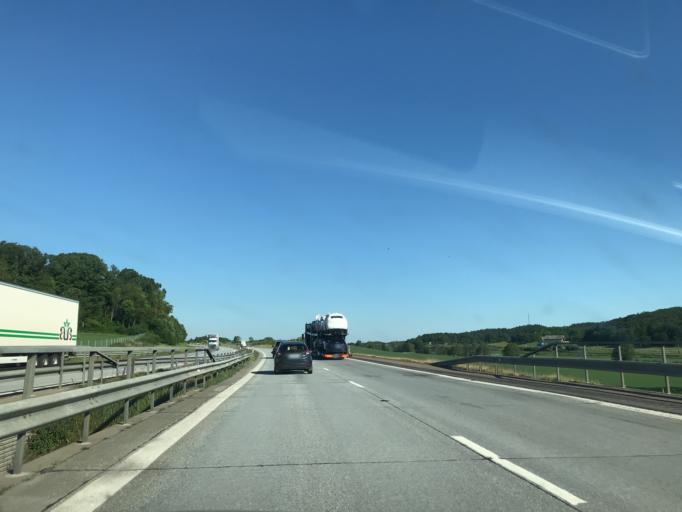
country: SE
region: Halland
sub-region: Halmstads Kommun
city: Getinge
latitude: 56.8638
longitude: 12.6603
